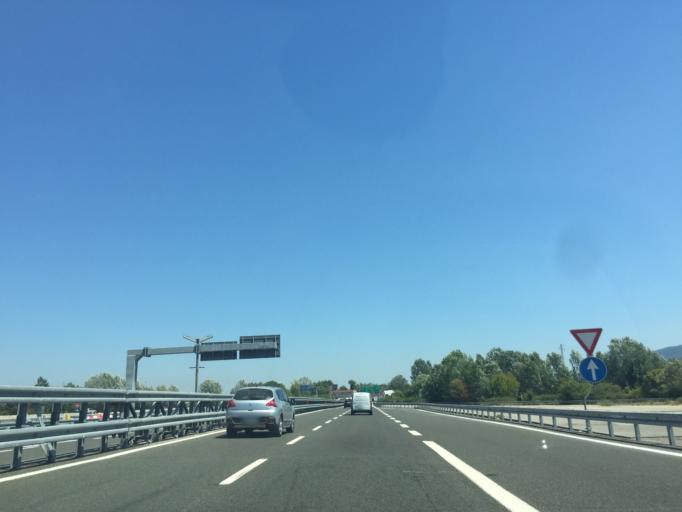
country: IT
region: Tuscany
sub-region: Provincia di Lucca
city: Lucca
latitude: 43.8368
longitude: 10.4686
